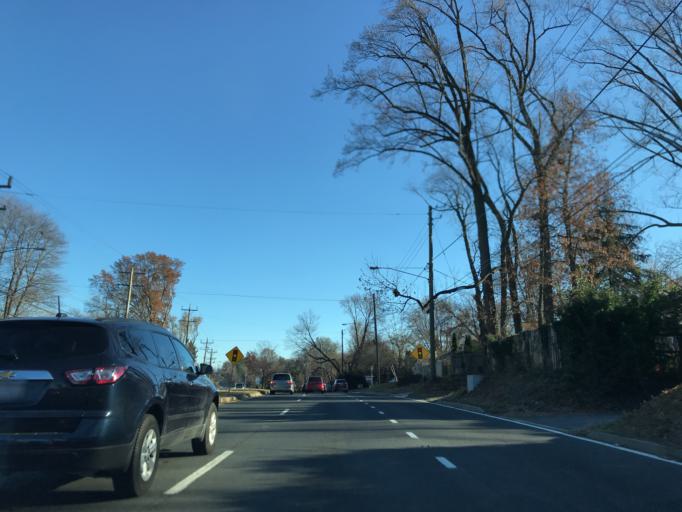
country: US
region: Maryland
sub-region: Montgomery County
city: Wheaton
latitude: 39.0466
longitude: -77.0674
